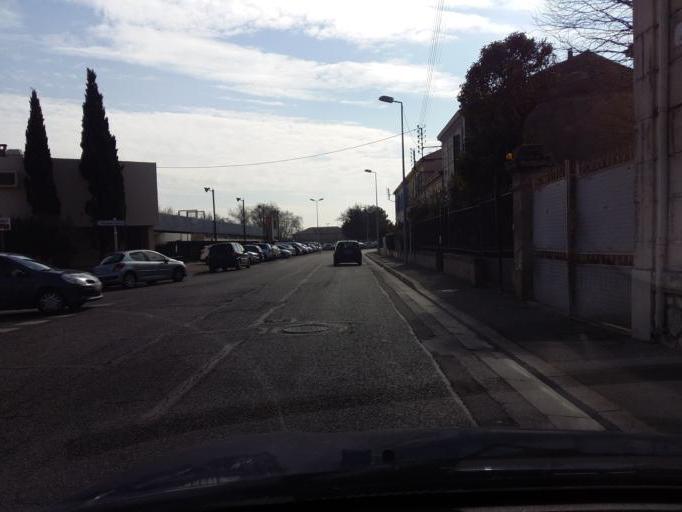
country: FR
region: Provence-Alpes-Cote d'Azur
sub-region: Departement des Bouches-du-Rhone
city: Salon-de-Provence
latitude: 43.6371
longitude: 5.0906
